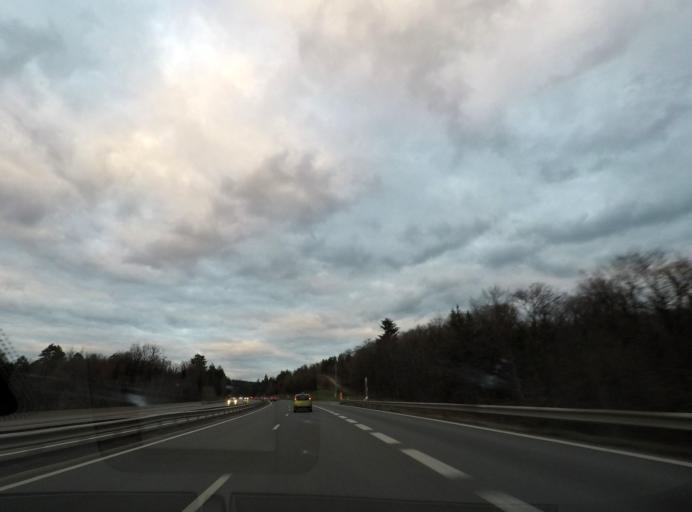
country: FR
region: Rhone-Alpes
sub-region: Departement de l'Ain
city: Poncin
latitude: 46.1078
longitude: 5.4604
